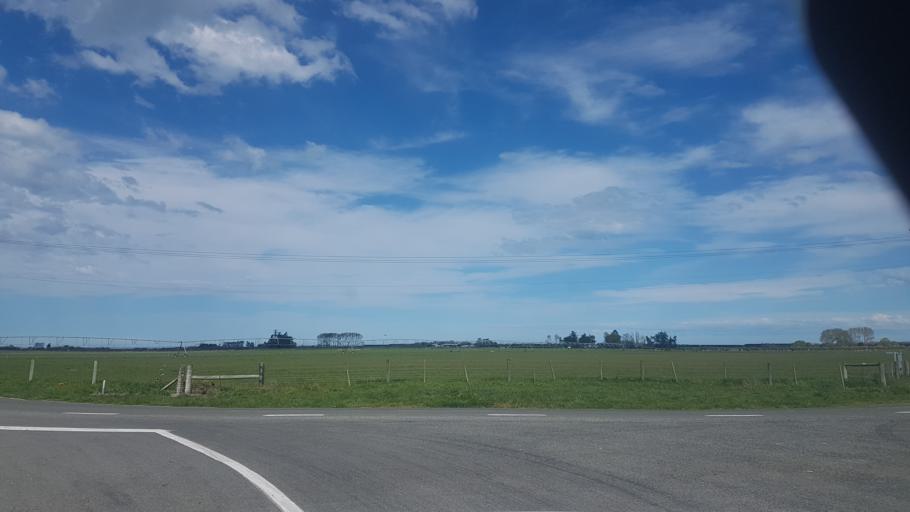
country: NZ
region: Canterbury
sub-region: Timaru District
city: Timaru
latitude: -44.2231
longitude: 171.3546
